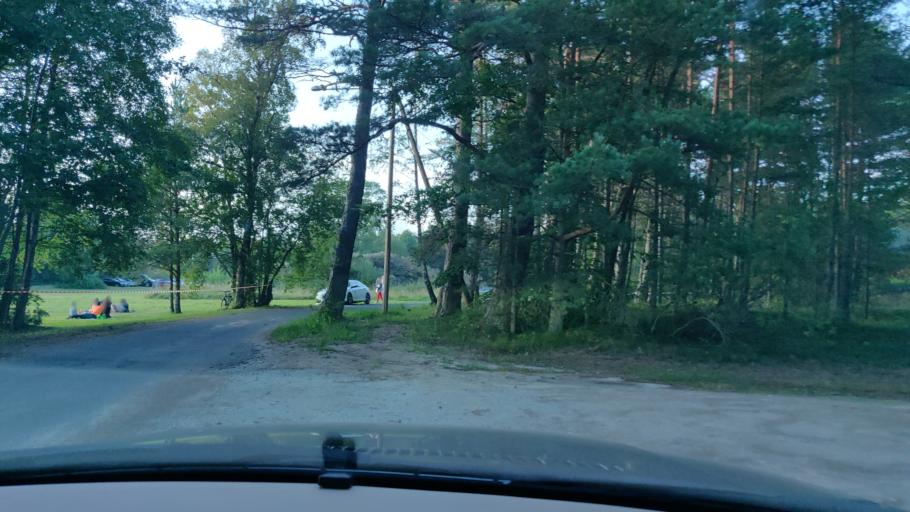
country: EE
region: Harju
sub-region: Keila linn
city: Keila
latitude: 59.3459
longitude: 24.2482
